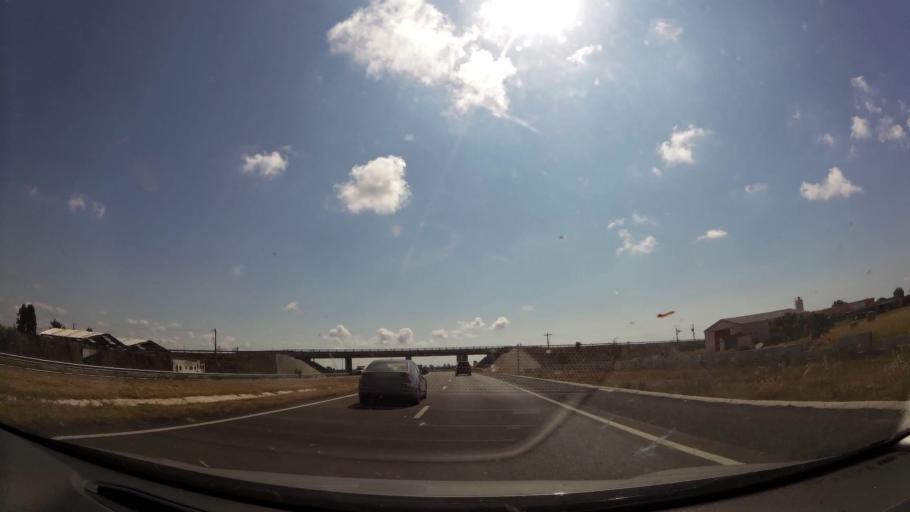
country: MA
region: Rabat-Sale-Zemmour-Zaer
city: Skhirat
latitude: 33.8638
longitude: -6.9639
